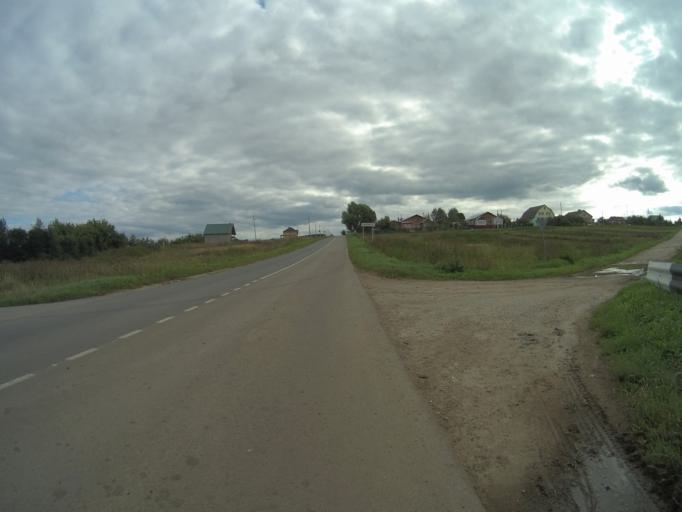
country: RU
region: Vladimir
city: Bogolyubovo
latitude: 56.2745
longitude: 40.5275
